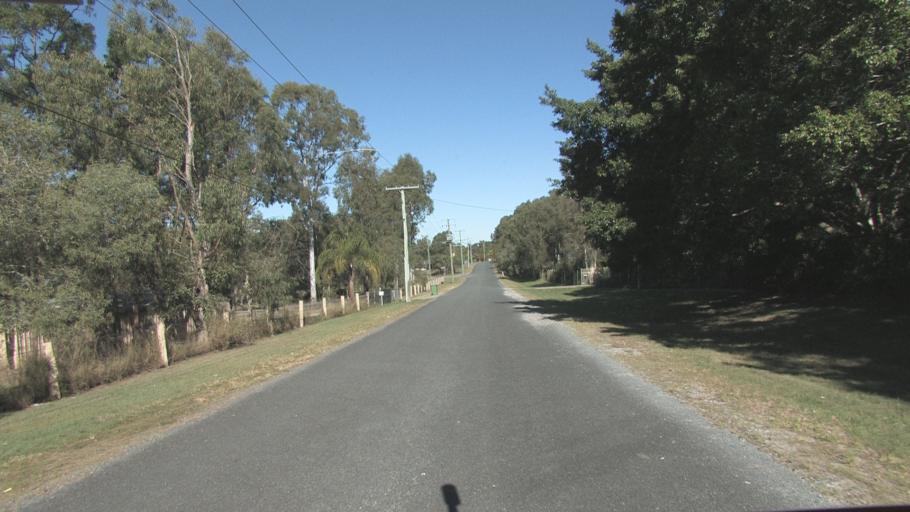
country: AU
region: Queensland
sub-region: Logan
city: Park Ridge South
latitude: -27.7118
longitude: 153.0412
